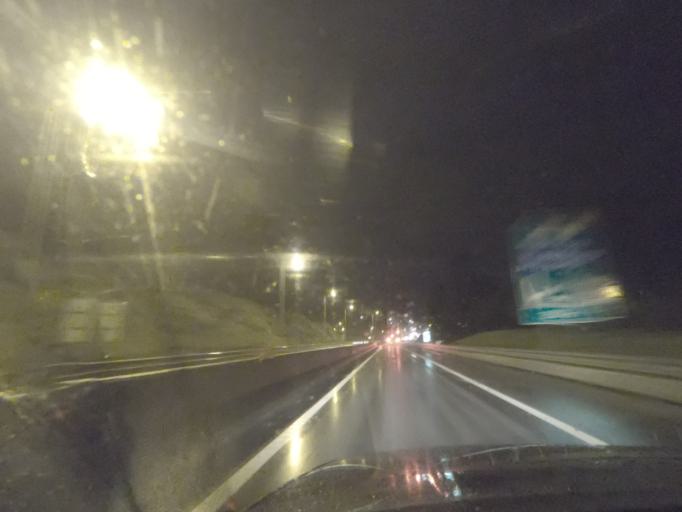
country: PT
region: Vila Real
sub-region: Vila Real
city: Vila Real
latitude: 41.3063
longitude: -7.7509
